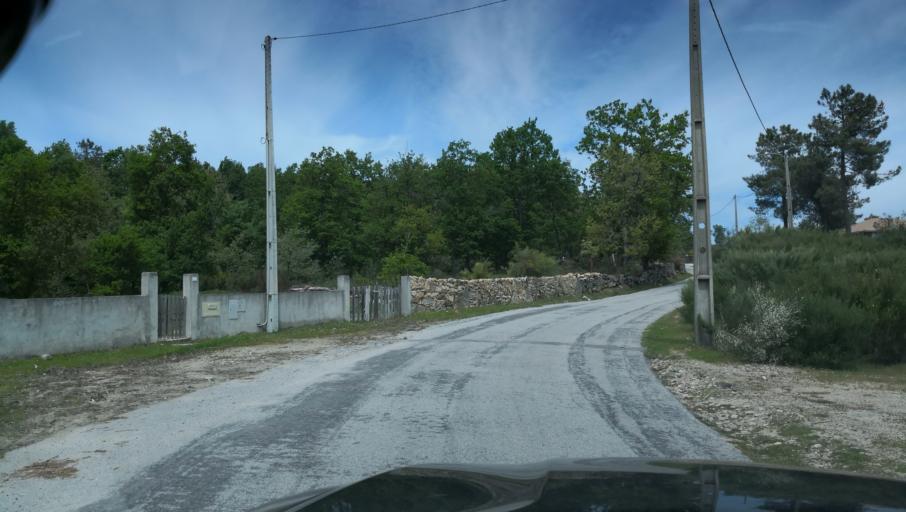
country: PT
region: Vila Real
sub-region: Vila Real
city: Vila Real
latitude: 41.2878
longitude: -7.8068
